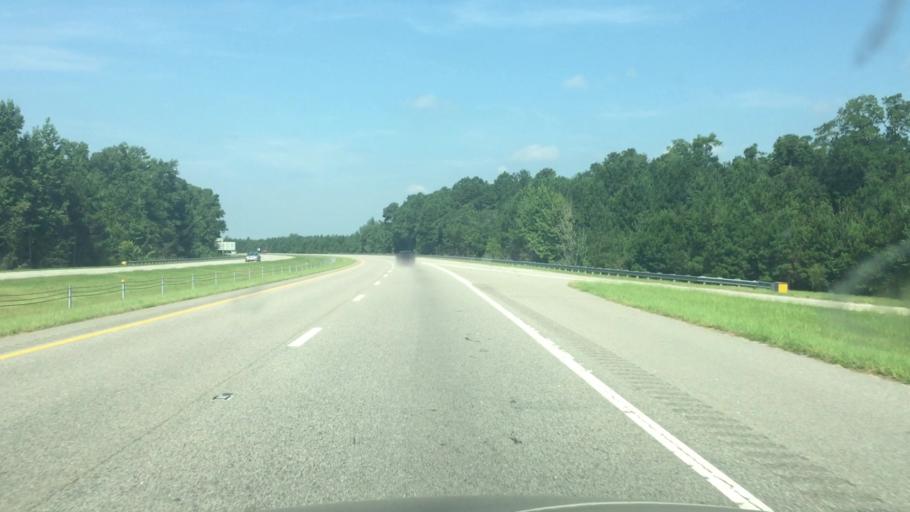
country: US
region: North Carolina
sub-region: Robeson County
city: Pembroke
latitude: 34.5987
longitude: -79.1365
